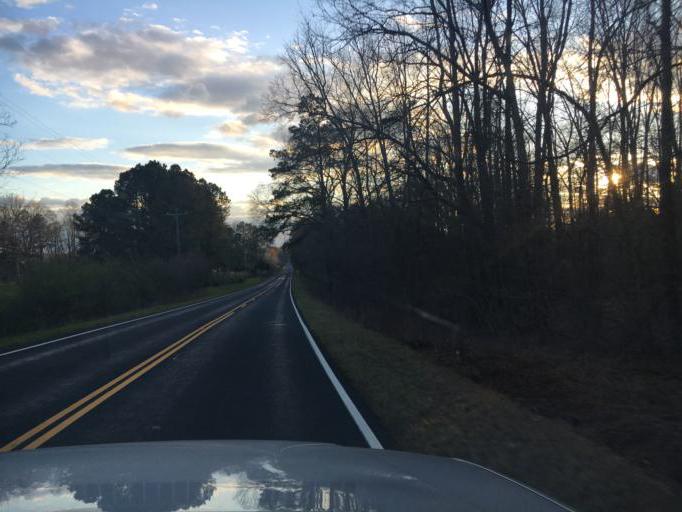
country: US
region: South Carolina
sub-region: Greenwood County
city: Greenwood
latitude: 34.0925
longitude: -82.1917
